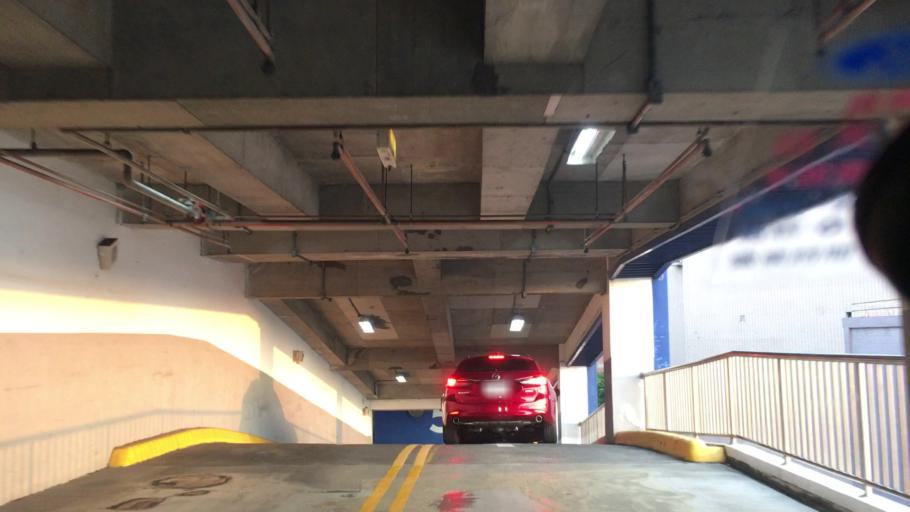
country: TW
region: Taiwan
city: Taoyuan City
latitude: 24.9899
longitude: 121.2865
